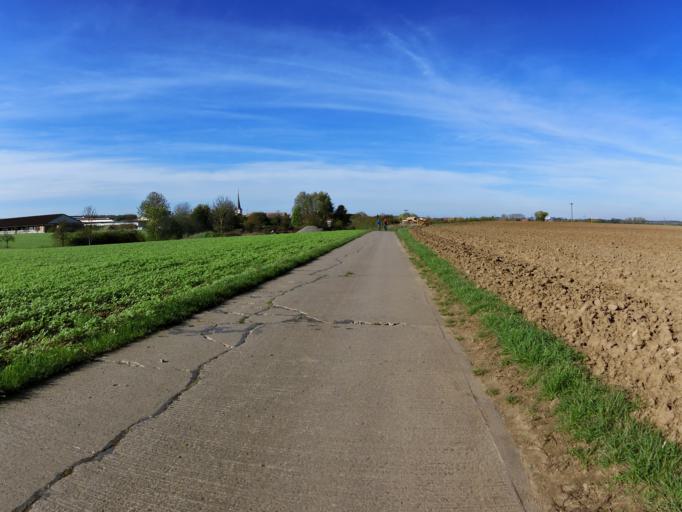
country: DE
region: Bavaria
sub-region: Regierungsbezirk Unterfranken
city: Biebelried
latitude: 49.7256
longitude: 10.0941
